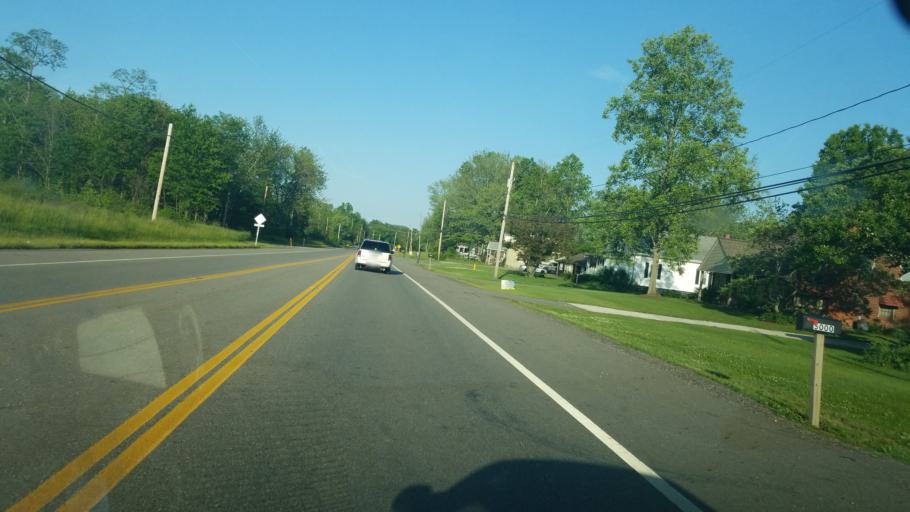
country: US
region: Ohio
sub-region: Portage County
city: Ravenna
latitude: 41.1568
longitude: -81.2135
